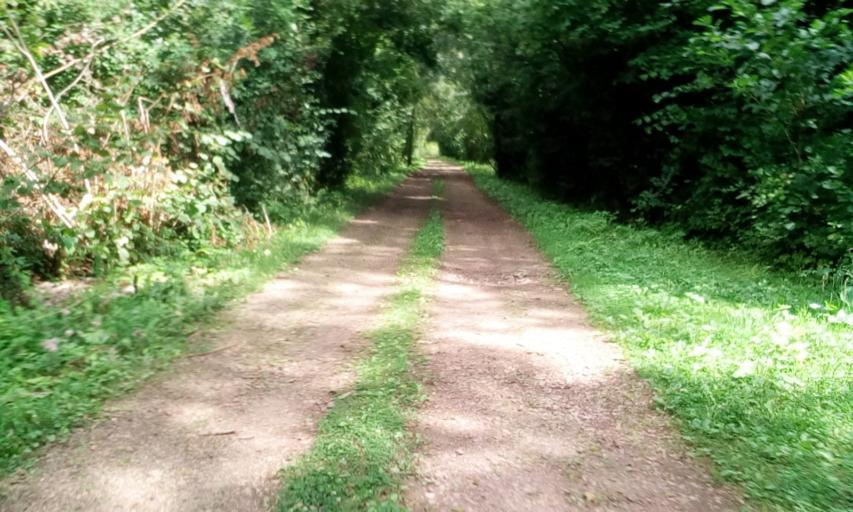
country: FR
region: Lower Normandy
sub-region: Departement du Calvados
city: Bellengreville
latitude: 49.1142
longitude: -0.2204
